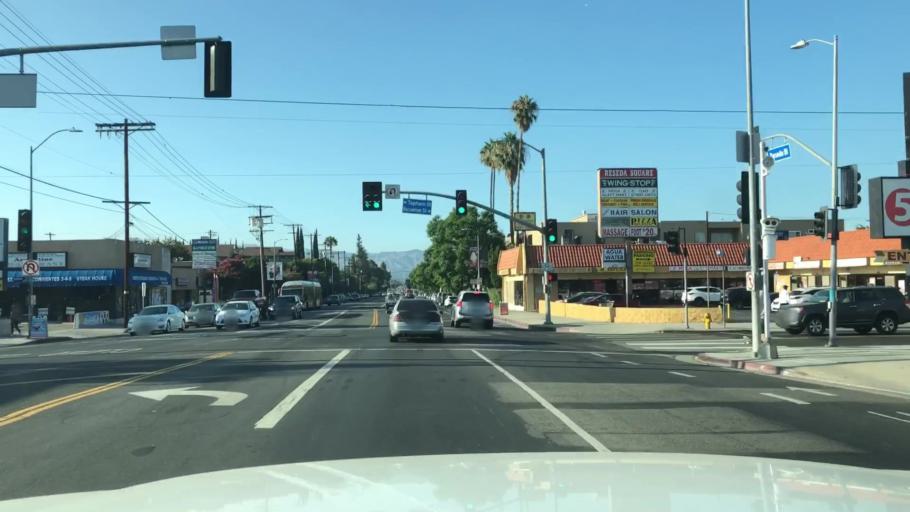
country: US
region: California
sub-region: Los Angeles County
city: Northridge
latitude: 34.1805
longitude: -118.5359
